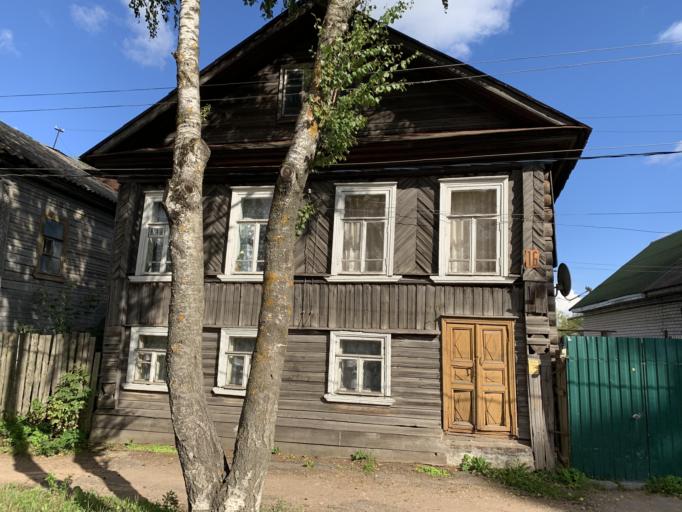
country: RU
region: Tverskaya
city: Vyshniy Volochek
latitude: 57.5755
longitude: 34.5552
